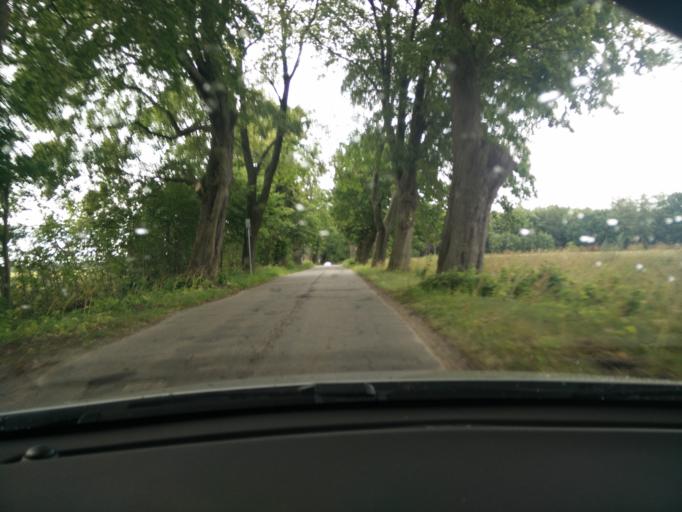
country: PL
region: Pomeranian Voivodeship
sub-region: Powiat pucki
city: Mrzezino
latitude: 54.6743
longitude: 18.4585
